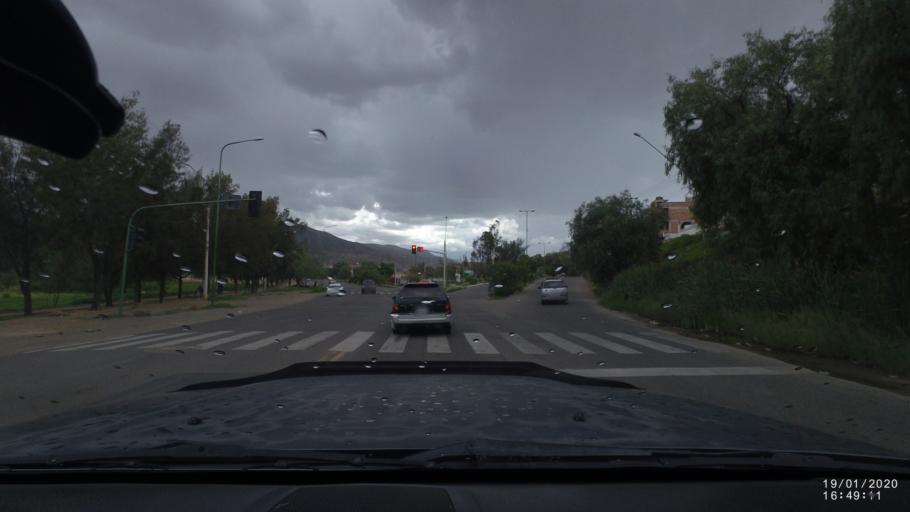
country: BO
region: Cochabamba
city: Cochabamba
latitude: -17.4157
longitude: -66.1414
